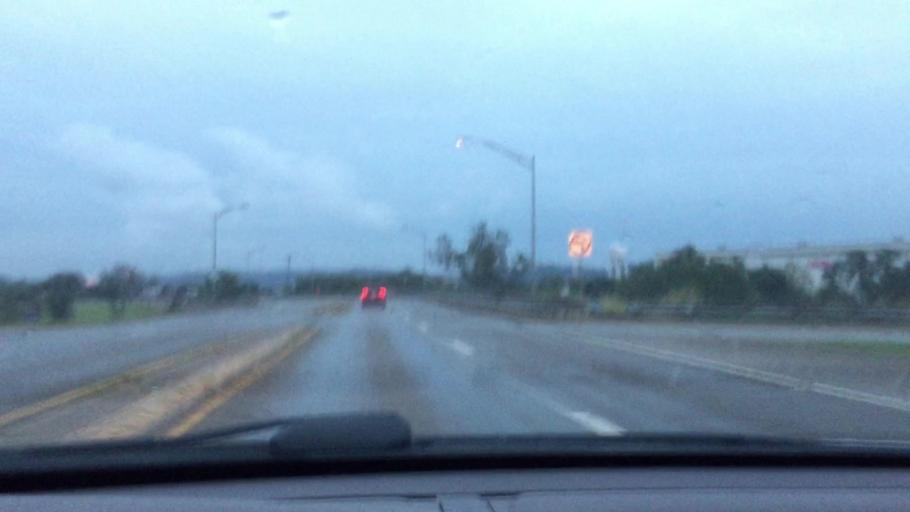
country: US
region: Pennsylvania
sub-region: Allegheny County
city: Cheswick
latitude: 40.5558
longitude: -79.8132
